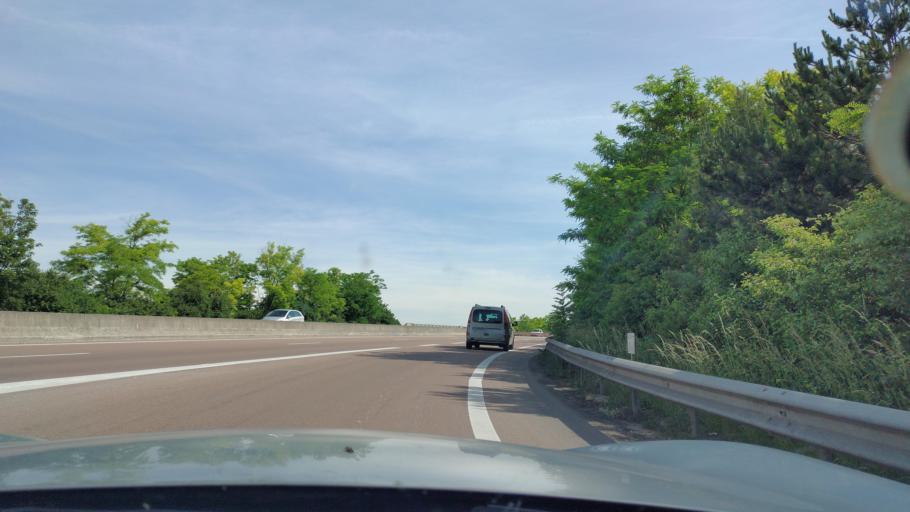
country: FR
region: Champagne-Ardenne
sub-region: Departement de l'Aube
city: La Chapelle-Saint-Luc
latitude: 48.3253
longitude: 4.0289
